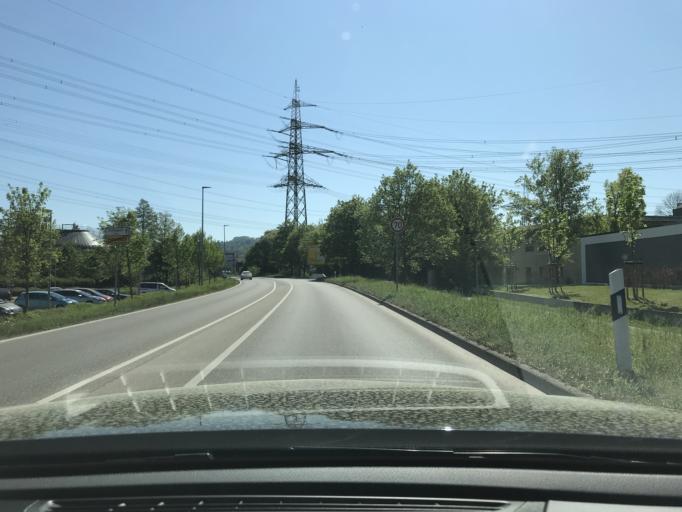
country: DE
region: Baden-Wuerttemberg
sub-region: Regierungsbezirk Stuttgart
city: Weinstadt-Endersbach
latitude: 48.8135
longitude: 9.3767
